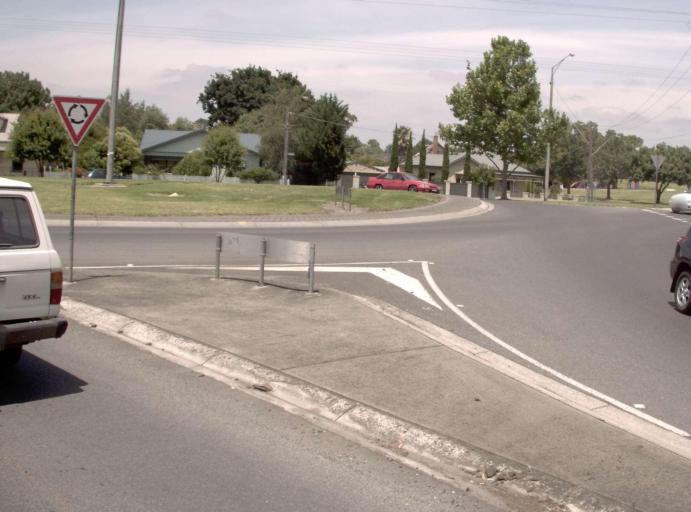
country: AU
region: Victoria
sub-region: Latrobe
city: Traralgon
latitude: -38.2001
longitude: 146.5333
